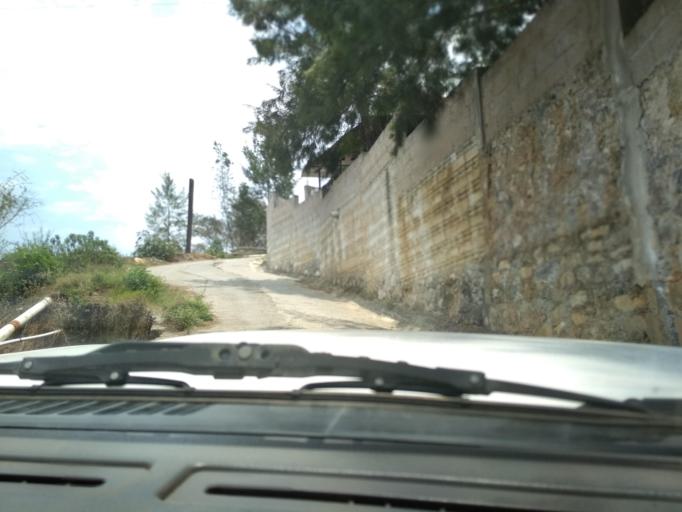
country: MX
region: Veracruz
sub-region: Camerino Z. Mendoza
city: La Cuesta
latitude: 18.7937
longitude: -97.1766
